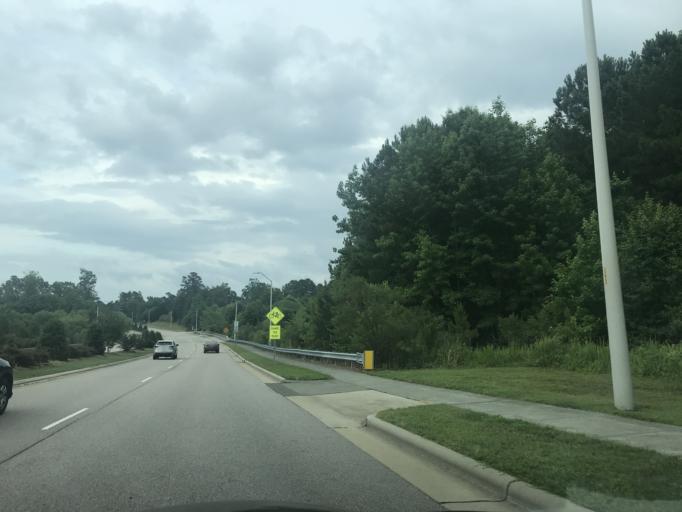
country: US
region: North Carolina
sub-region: Wake County
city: Morrisville
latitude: 35.8130
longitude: -78.8644
